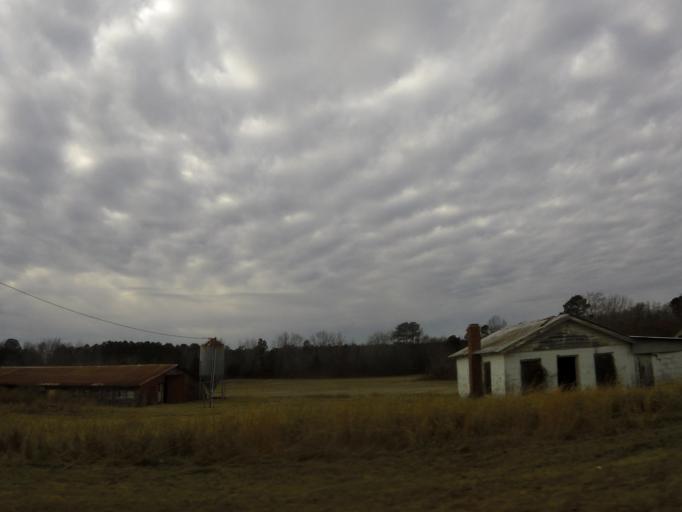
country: US
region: North Carolina
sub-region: Hertford County
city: Murfreesboro
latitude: 36.4273
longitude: -77.1420
